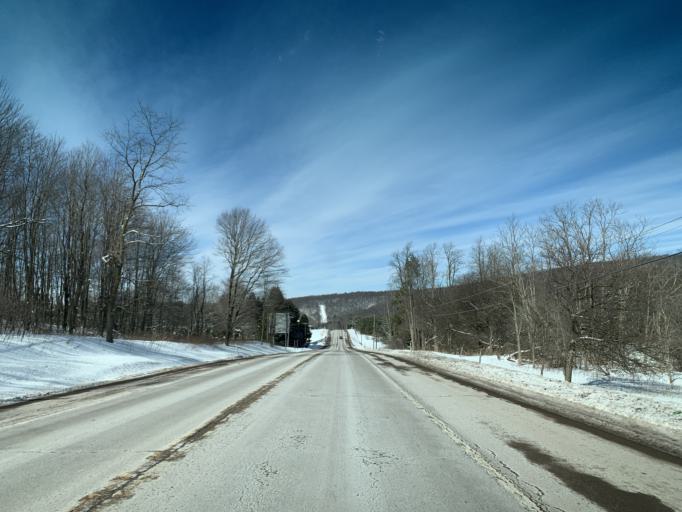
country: US
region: Pennsylvania
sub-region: Somerset County
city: Meyersdale
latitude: 39.7147
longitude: -79.2830
